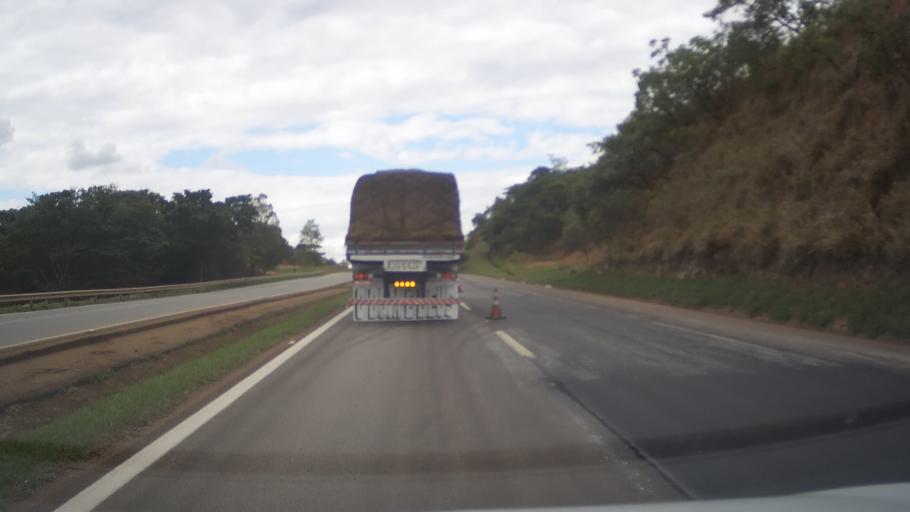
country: BR
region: Minas Gerais
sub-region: Itauna
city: Itauna
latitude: -20.3182
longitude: -44.4544
